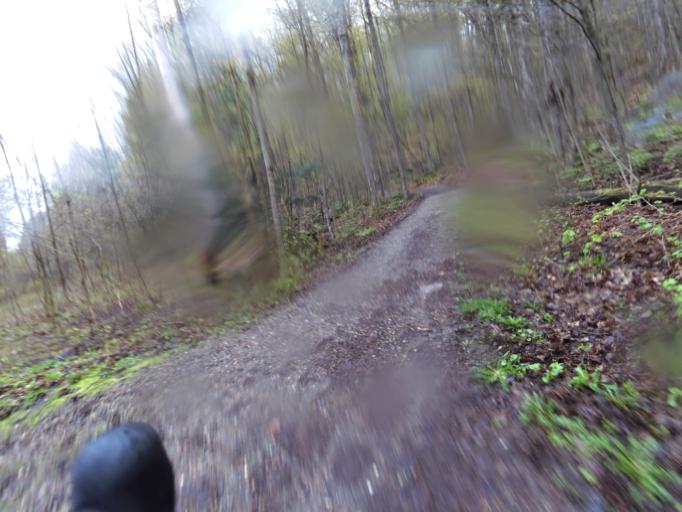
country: CA
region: Quebec
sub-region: Outaouais
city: Gatineau
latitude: 45.5044
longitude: -75.8166
